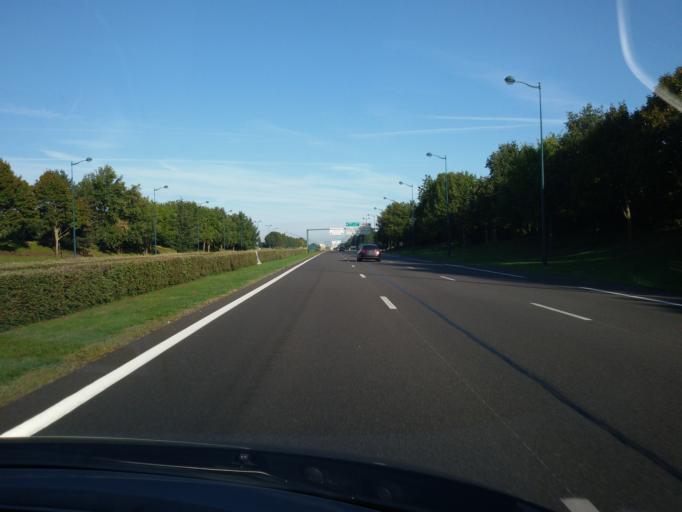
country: FR
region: Ile-de-France
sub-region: Departement de Seine-et-Marne
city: Bailly-Romainvilliers
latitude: 48.8459
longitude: 2.8117
